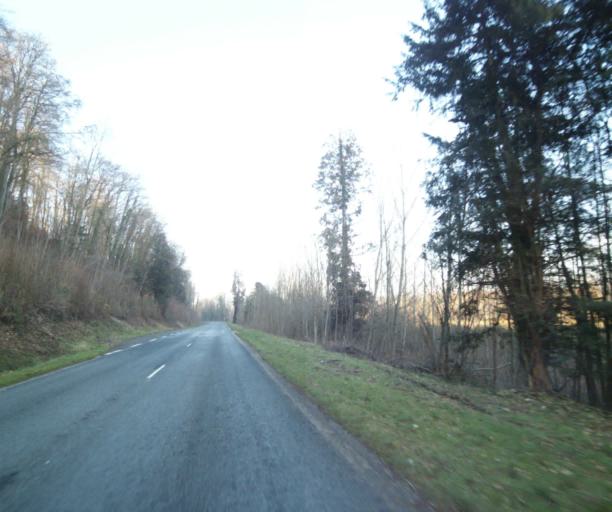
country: FR
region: Champagne-Ardenne
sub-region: Departement de la Haute-Marne
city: Bienville
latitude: 48.5756
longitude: 5.0384
